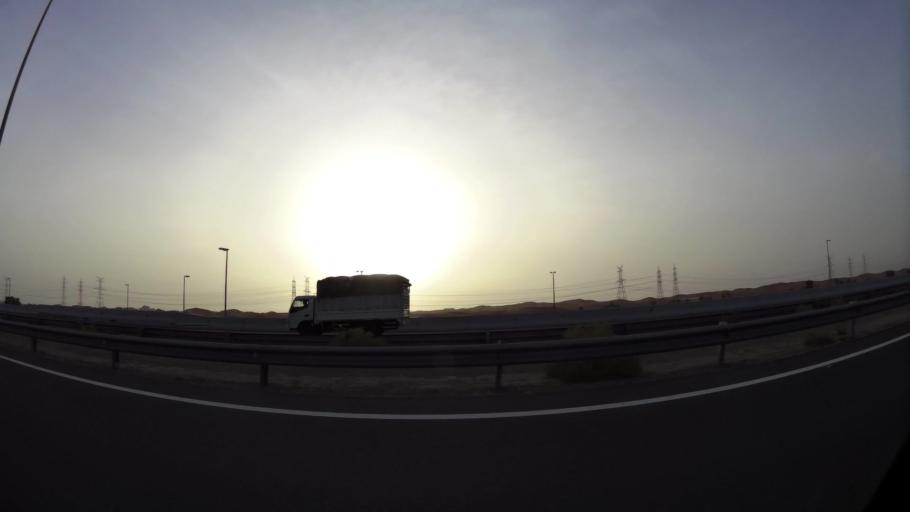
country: OM
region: Al Buraimi
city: Al Buraymi
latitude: 24.2986
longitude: 55.7406
